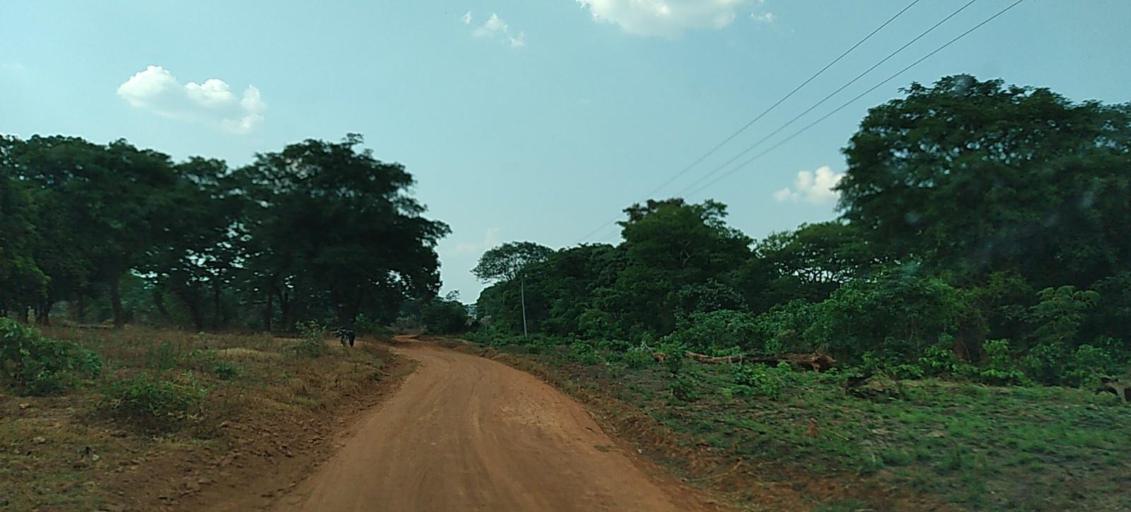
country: ZM
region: Copperbelt
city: Mpongwe
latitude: -13.5151
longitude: 28.0991
